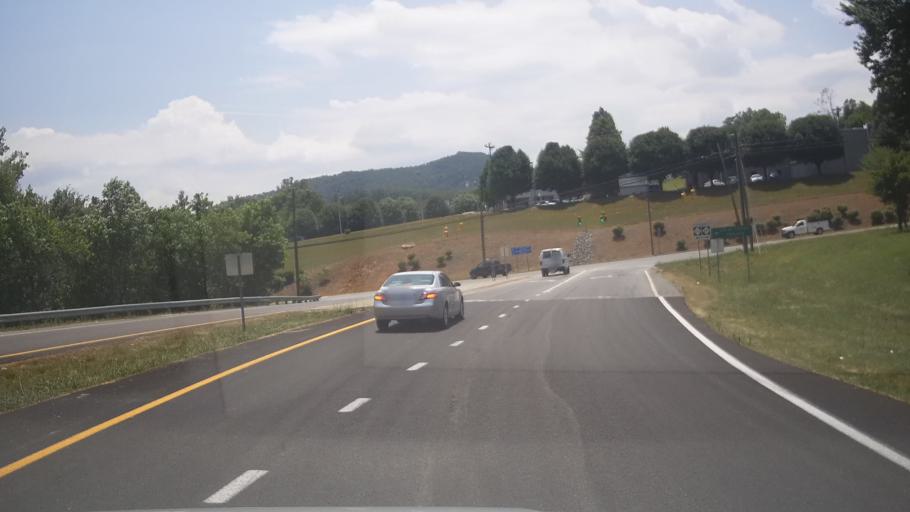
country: US
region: North Carolina
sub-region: McDowell County
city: Marion
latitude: 35.6582
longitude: -81.9607
